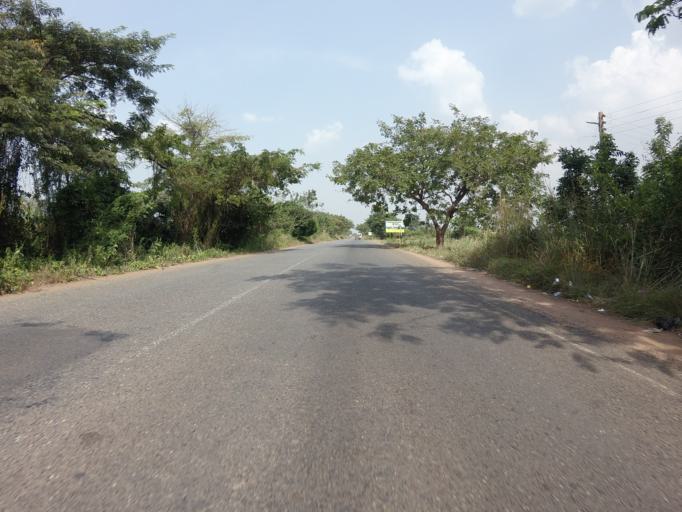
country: GH
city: Akropong
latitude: 5.9284
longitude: -0.0431
